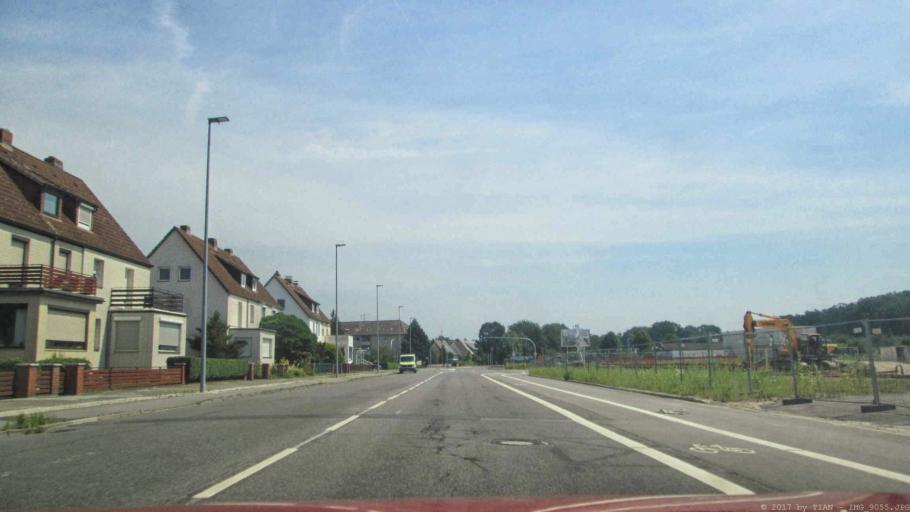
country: DE
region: Lower Saxony
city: Wolfsburg
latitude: 52.4224
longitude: 10.8090
